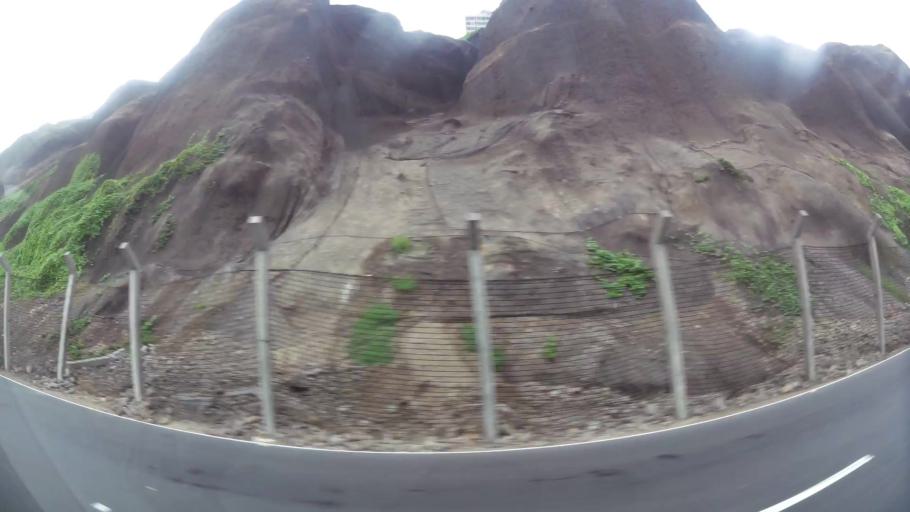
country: PE
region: Lima
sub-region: Lima
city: San Isidro
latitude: -12.1309
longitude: -77.0340
